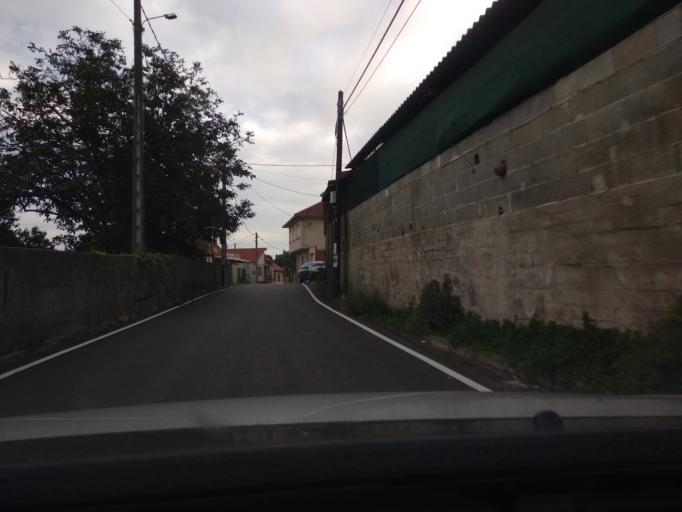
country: ES
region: Galicia
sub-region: Provincia de Pontevedra
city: Moana
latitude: 42.2926
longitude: -8.7388
